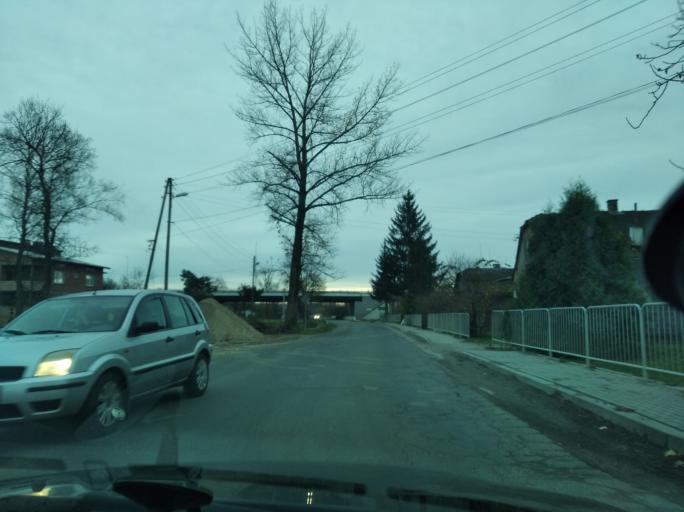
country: PL
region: Subcarpathian Voivodeship
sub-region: Powiat lancucki
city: Czarna
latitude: 50.0920
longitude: 22.1841
